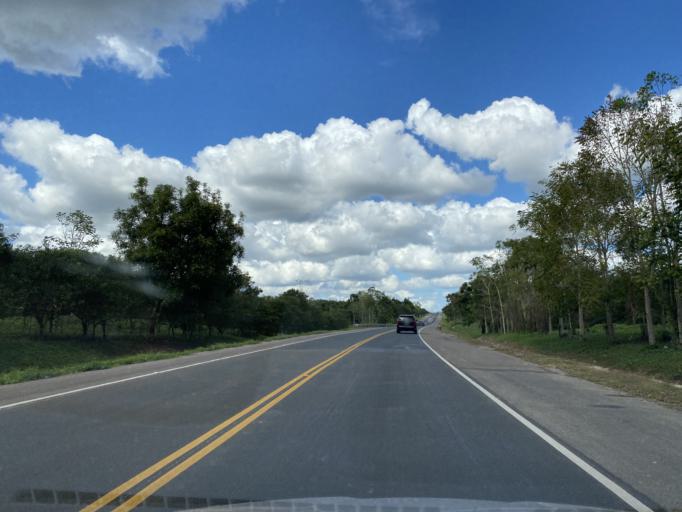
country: DO
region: Monte Plata
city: Monte Plata
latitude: 18.7212
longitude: -69.7603
